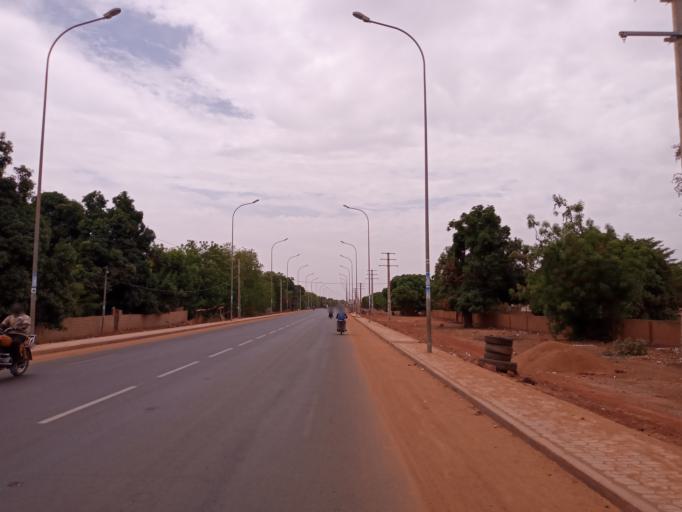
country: ML
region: Koulikoro
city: Koulikoro
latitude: 12.8510
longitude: -7.5717
